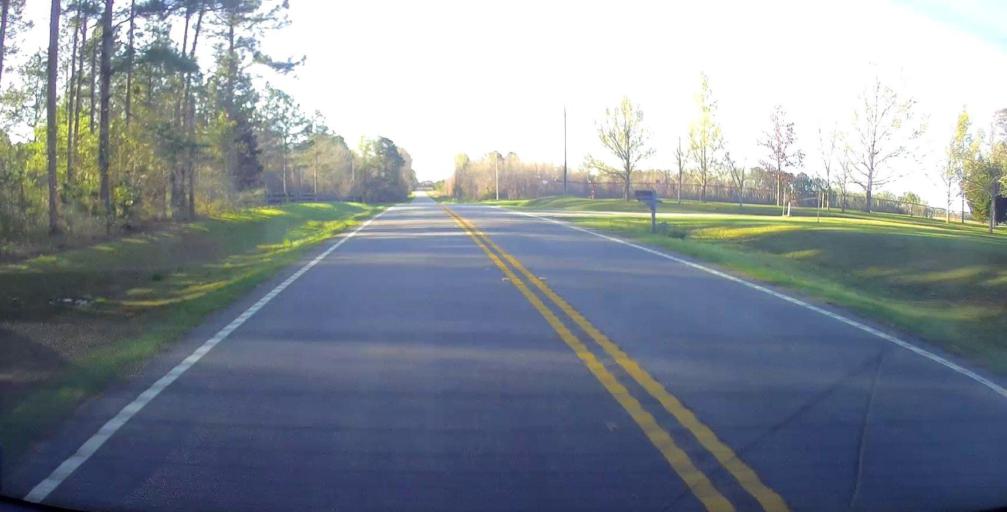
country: US
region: Georgia
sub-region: Pulaski County
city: Hawkinsville
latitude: 32.2221
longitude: -83.3890
